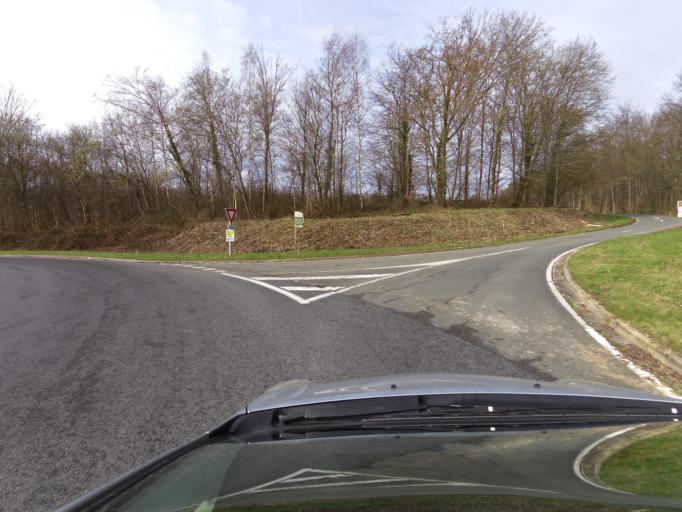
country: FR
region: Picardie
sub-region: Departement de l'Oise
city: Ver-sur-Launette
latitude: 49.1160
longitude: 2.6857
